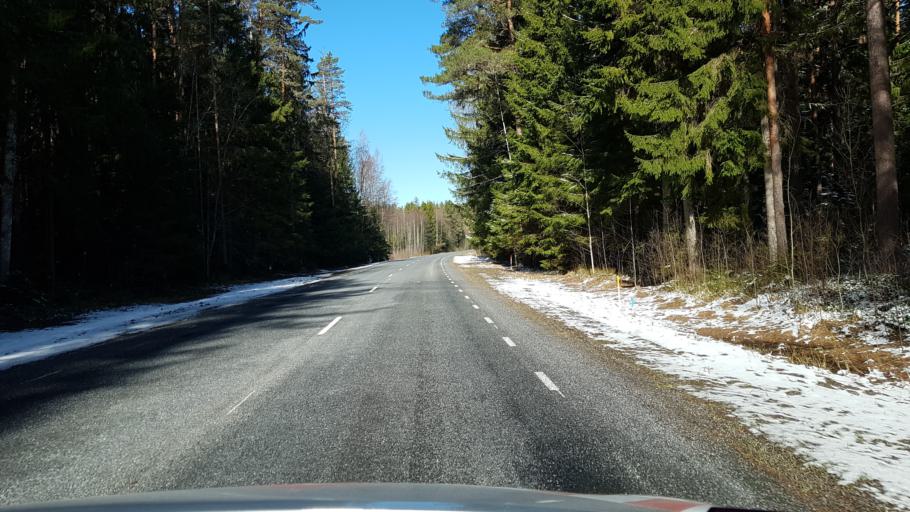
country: EE
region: Harju
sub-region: Loksa linn
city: Loksa
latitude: 59.5665
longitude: 25.9428
